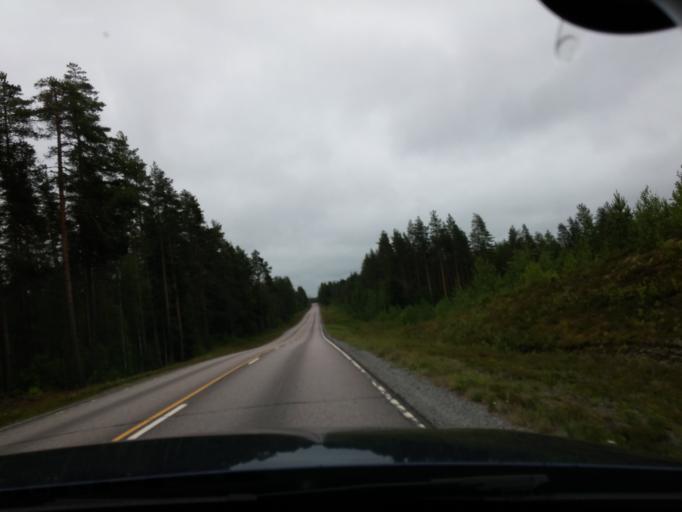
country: FI
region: Central Finland
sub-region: Saarijaervi-Viitasaari
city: Pylkoenmaeki
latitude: 62.6163
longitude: 24.7404
